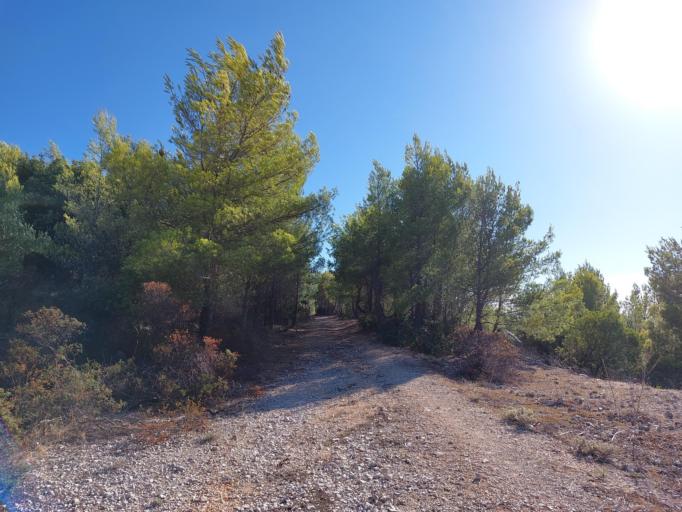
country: HR
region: Dubrovacko-Neretvanska
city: Smokvica
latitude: 42.7296
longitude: 16.8409
